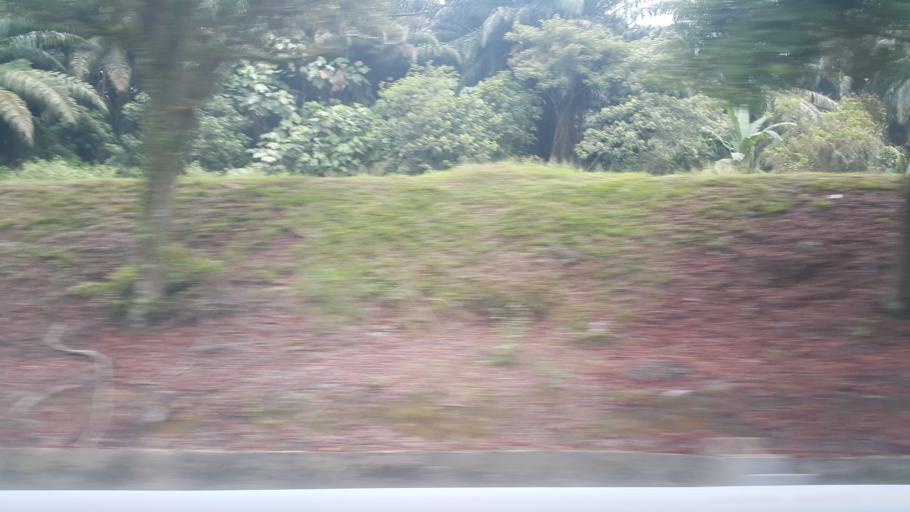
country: MY
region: Putrajaya
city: Putrajaya
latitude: 2.8474
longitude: 101.6599
